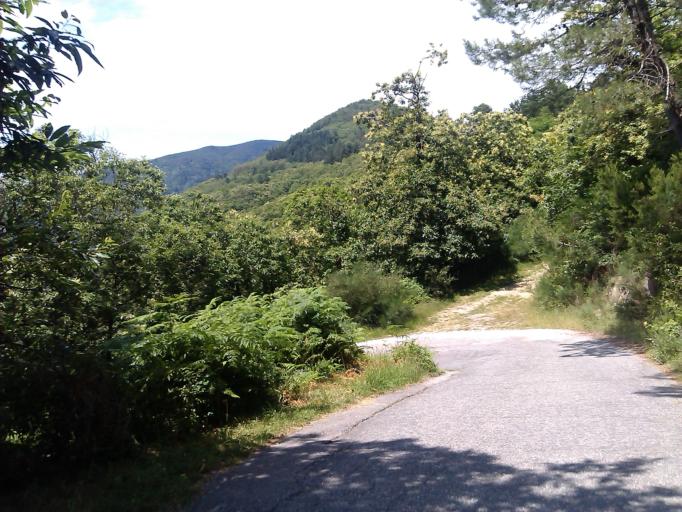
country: IT
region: Tuscany
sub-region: Provincia di Pistoia
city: Montale
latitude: 43.9699
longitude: 11.0373
